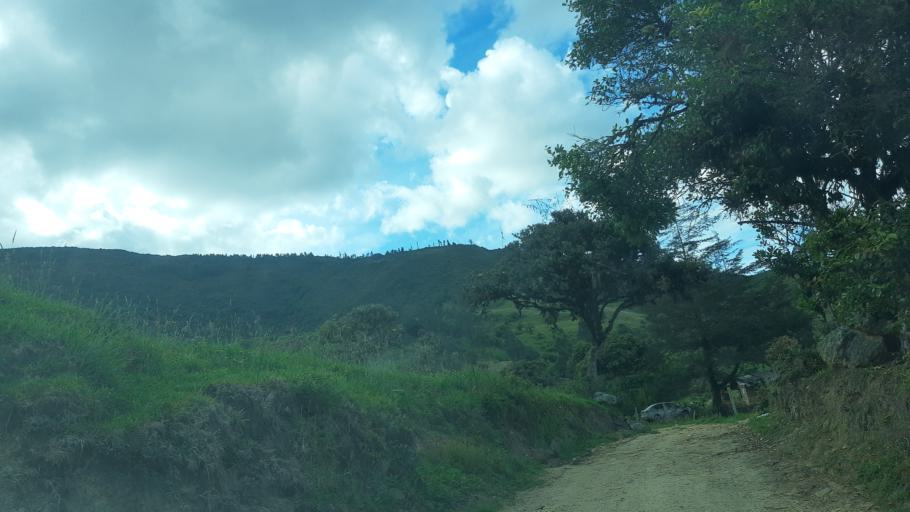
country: CO
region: Cundinamarca
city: Macheta
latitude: 5.0723
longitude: -73.6337
